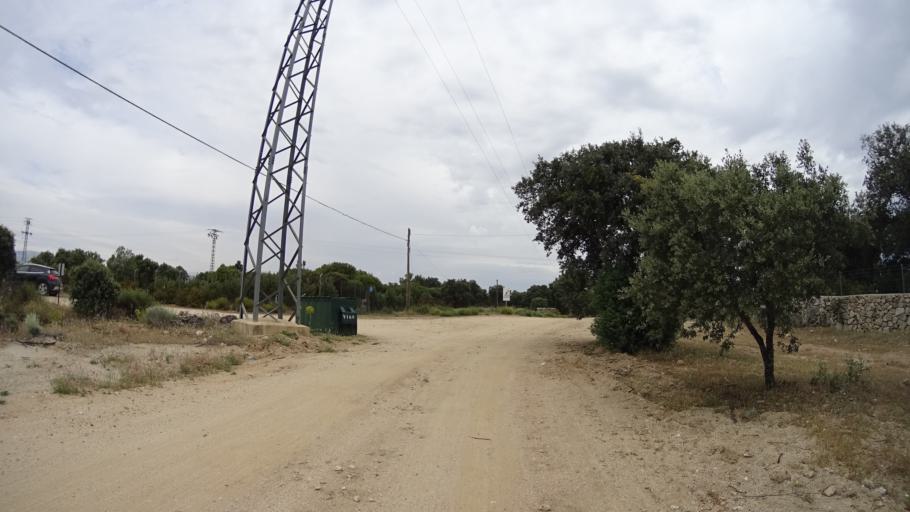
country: ES
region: Madrid
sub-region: Provincia de Madrid
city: Colmenarejo
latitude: 40.5471
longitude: -4.0385
